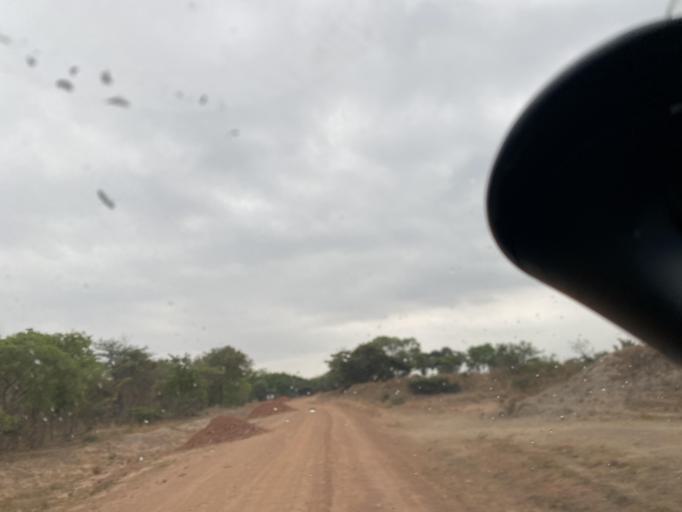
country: ZM
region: Lusaka
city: Chongwe
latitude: -15.1605
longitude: 28.7562
